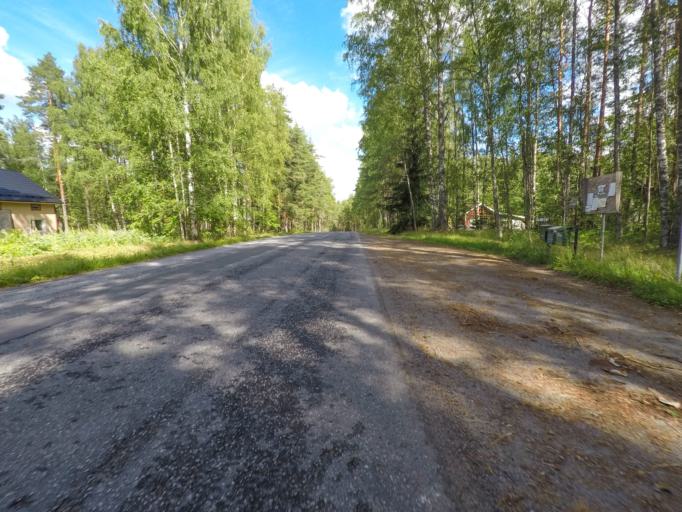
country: FI
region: South Karelia
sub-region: Lappeenranta
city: Joutseno
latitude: 61.1258
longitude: 28.3990
